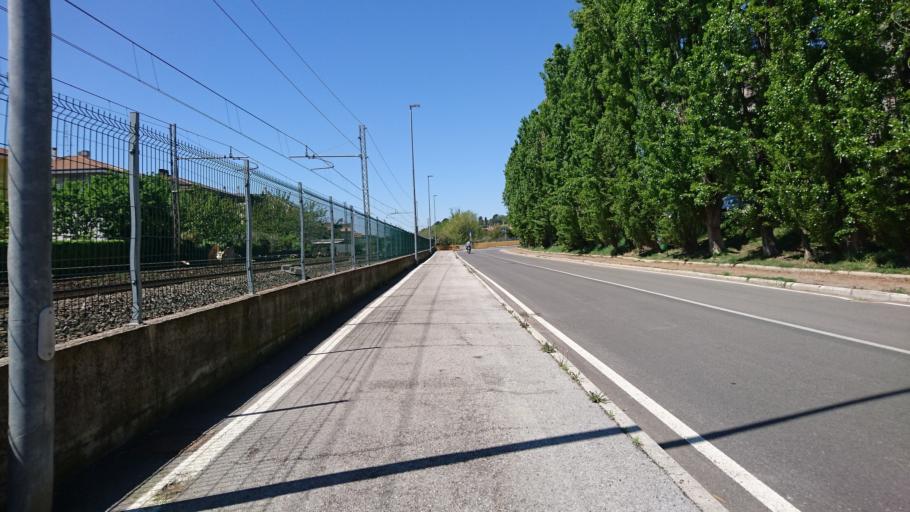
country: IT
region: The Marches
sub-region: Provincia di Pesaro e Urbino
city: Pesaro
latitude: 43.9092
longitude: 12.8907
